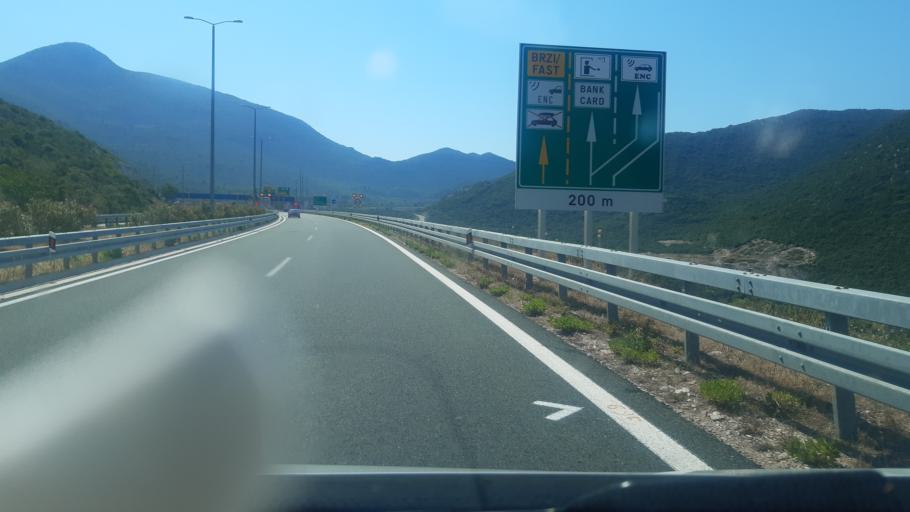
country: HR
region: Dubrovacko-Neretvanska
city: Komin
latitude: 43.1036
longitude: 17.4816
